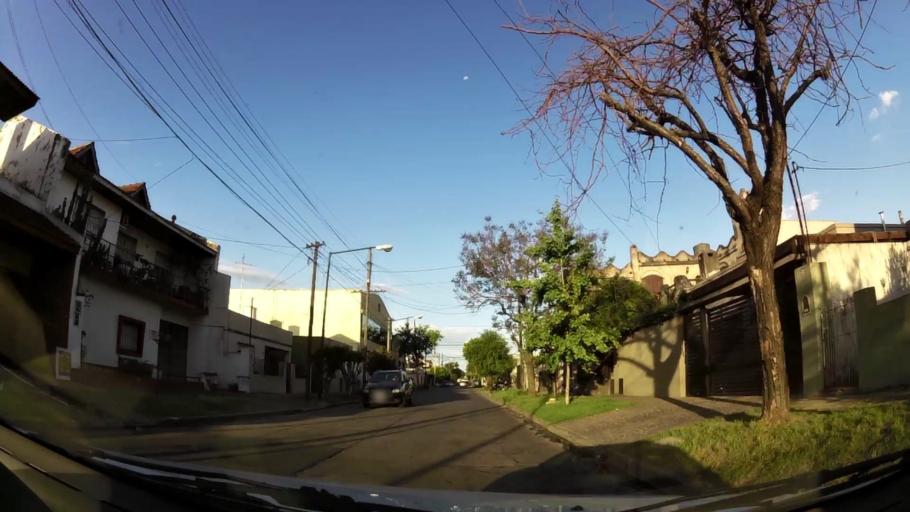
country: AR
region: Buenos Aires
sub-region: Partido de San Isidro
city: San Isidro
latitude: -34.4678
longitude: -58.5466
